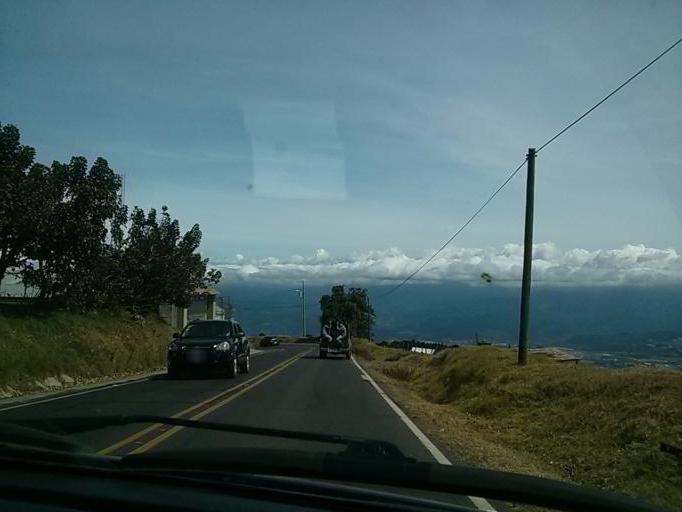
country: CR
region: Cartago
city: Cot
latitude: 9.9242
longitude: -83.8819
